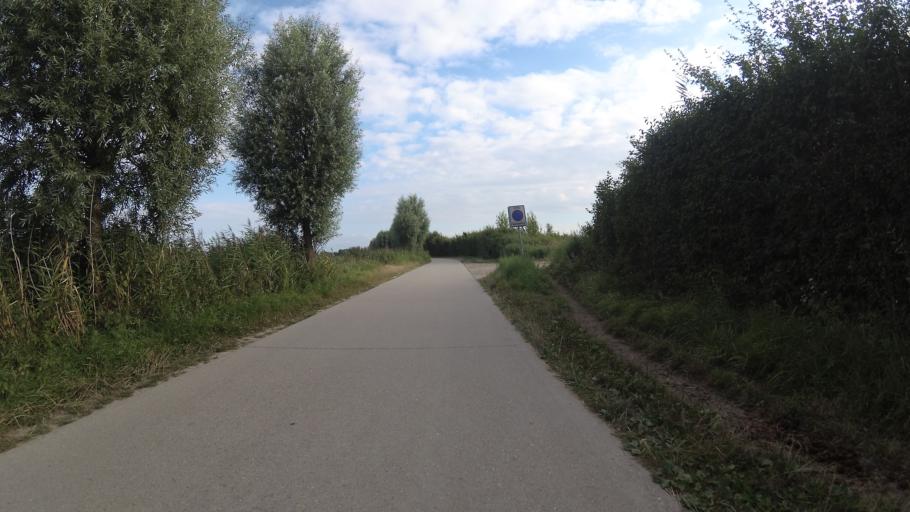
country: NL
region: Zeeland
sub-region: Gemeente Middelburg
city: Middelburg
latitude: 51.5663
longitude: 3.5231
